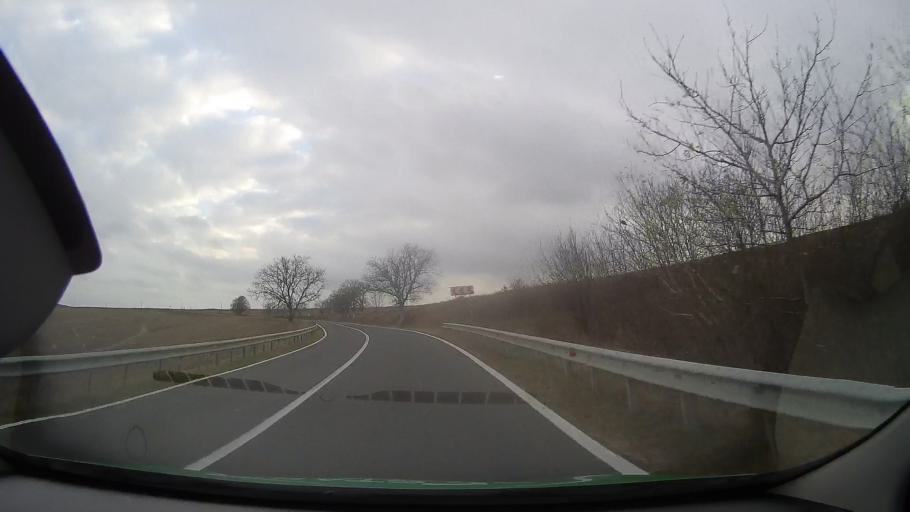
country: RO
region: Constanta
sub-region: Comuna Deleni
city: Deleni
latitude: 44.0973
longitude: 28.0172
